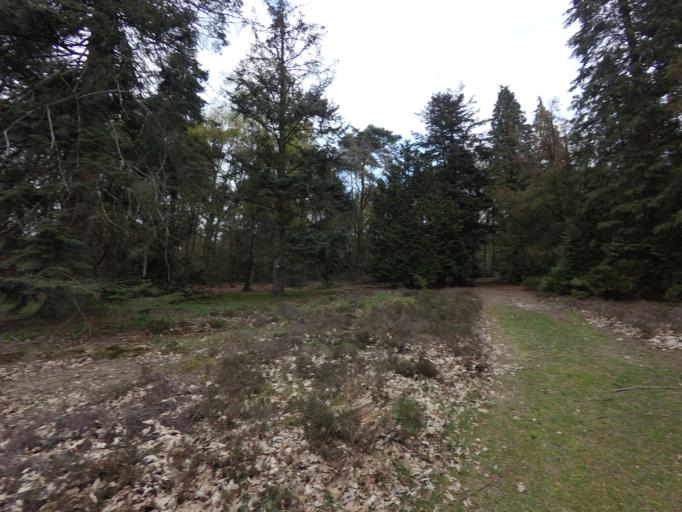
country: NL
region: Gelderland
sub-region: Gemeente Ede
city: Lunteren
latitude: 52.0904
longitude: 5.6440
